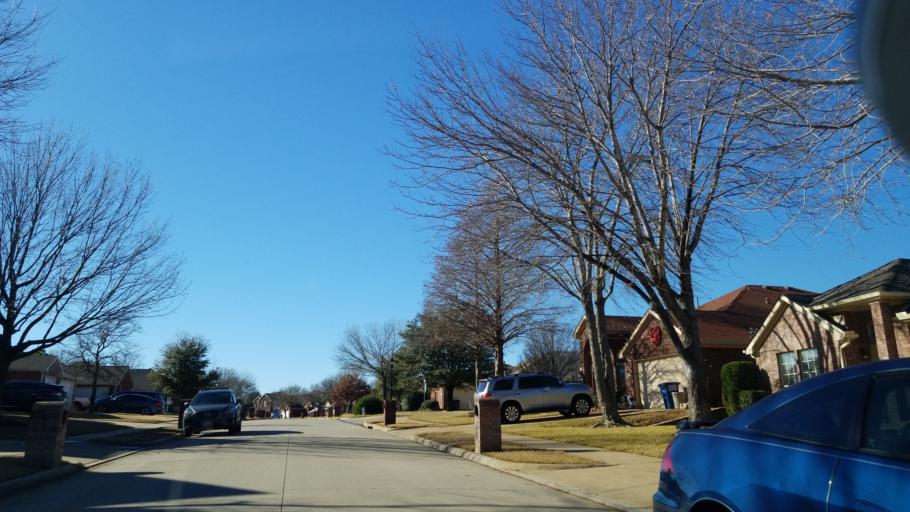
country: US
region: Texas
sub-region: Denton County
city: Corinth
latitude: 33.1408
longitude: -97.0827
